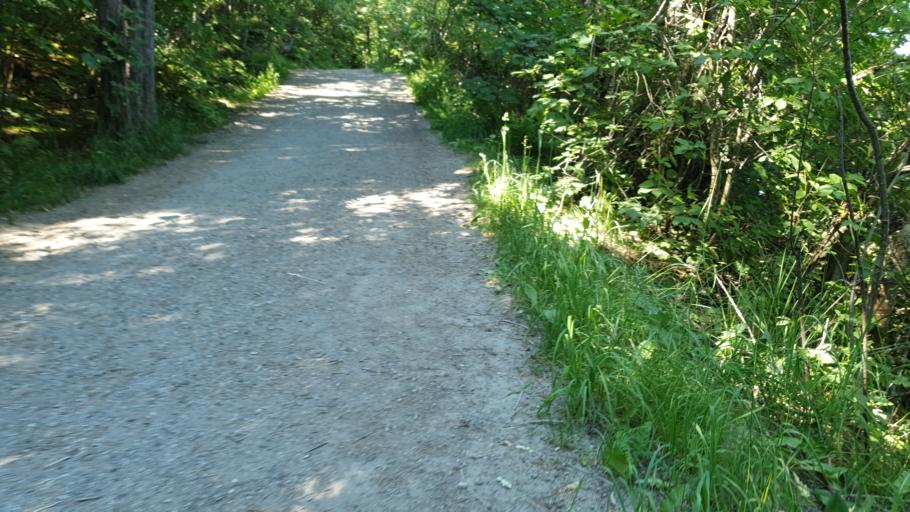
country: NO
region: Sor-Trondelag
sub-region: Trondheim
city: Trondheim
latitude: 63.4439
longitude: 10.4695
